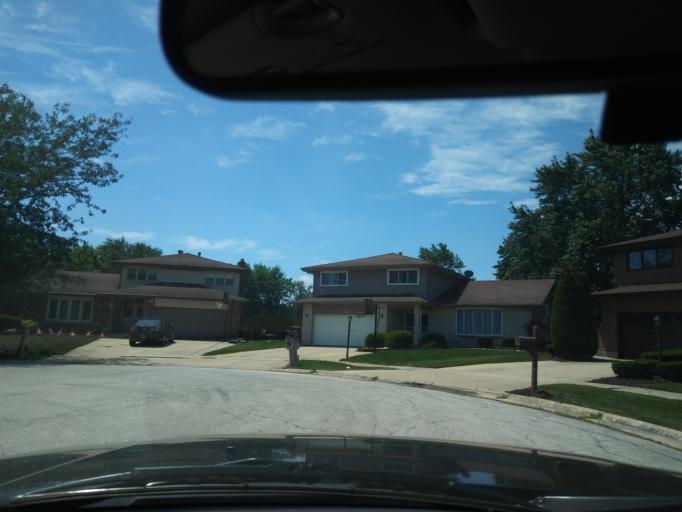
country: US
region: Illinois
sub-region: Cook County
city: Oak Forest
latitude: 41.6044
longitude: -87.7701
